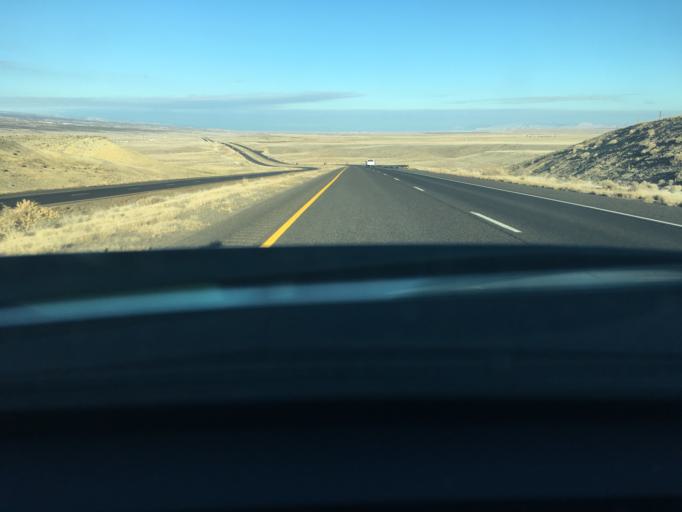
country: US
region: Colorado
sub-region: Mesa County
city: Palisade
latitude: 38.8523
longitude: -108.3080
